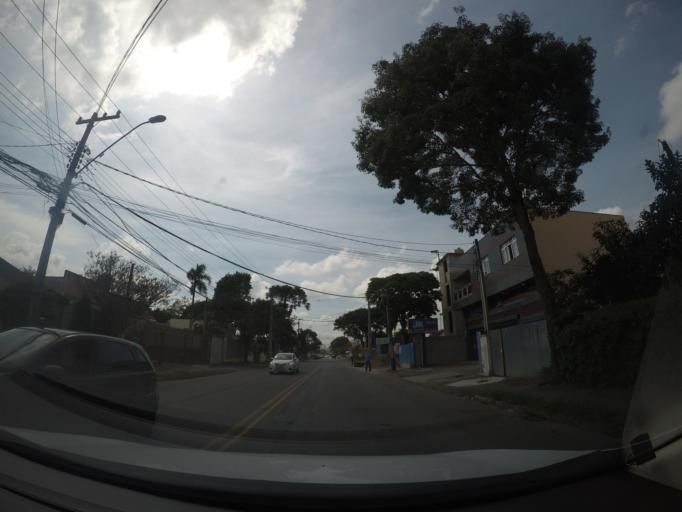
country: BR
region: Parana
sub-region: Curitiba
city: Curitiba
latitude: -25.4749
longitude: -49.2638
